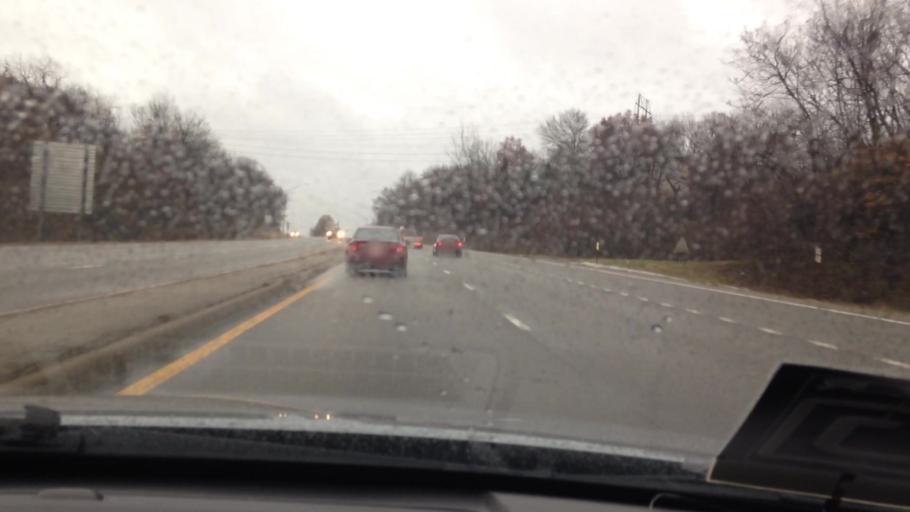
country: US
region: Kansas
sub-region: Johnson County
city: Roeland Park
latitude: 39.0464
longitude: -94.6457
